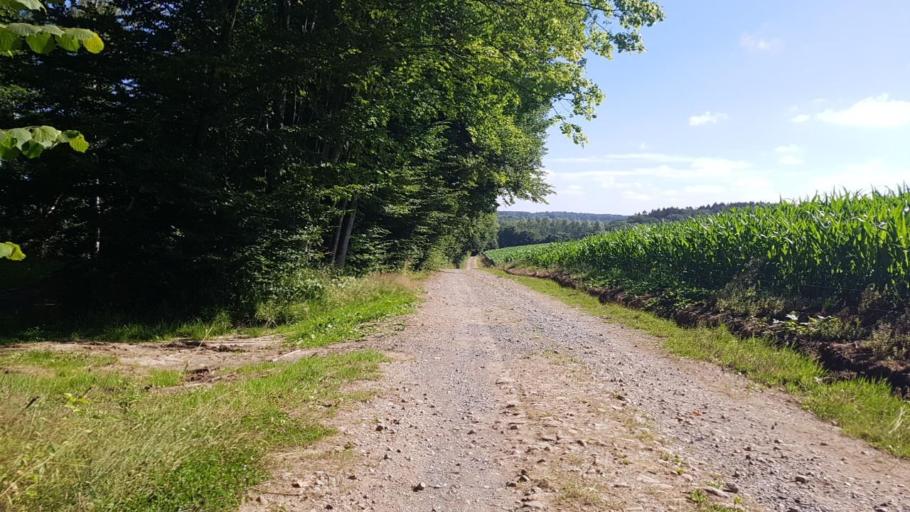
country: FR
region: Nord-Pas-de-Calais
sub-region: Departement du Nord
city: Anor
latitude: 49.9695
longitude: 4.1172
